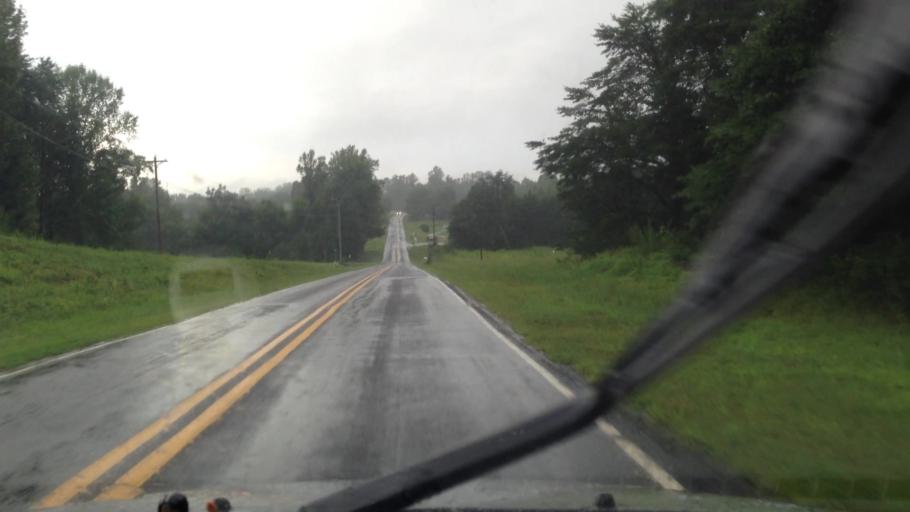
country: US
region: North Carolina
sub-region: Guilford County
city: Stokesdale
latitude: 36.2128
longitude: -80.0287
